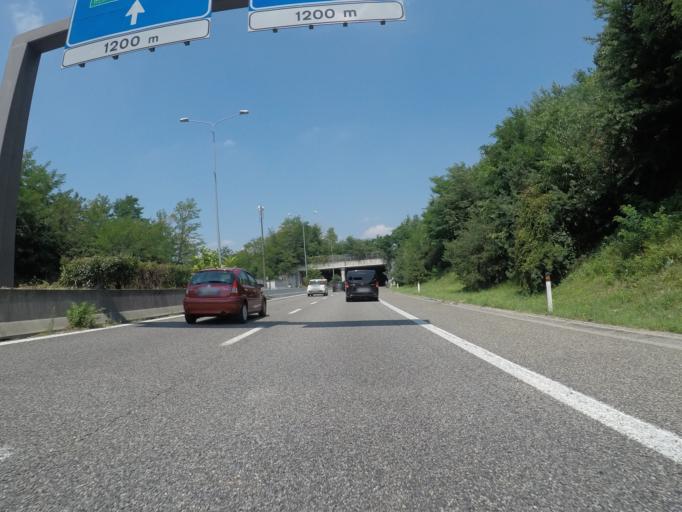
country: IT
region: Lombardy
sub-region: Provincia di Varese
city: Vizzola Ticino
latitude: 45.6328
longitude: 8.7024
